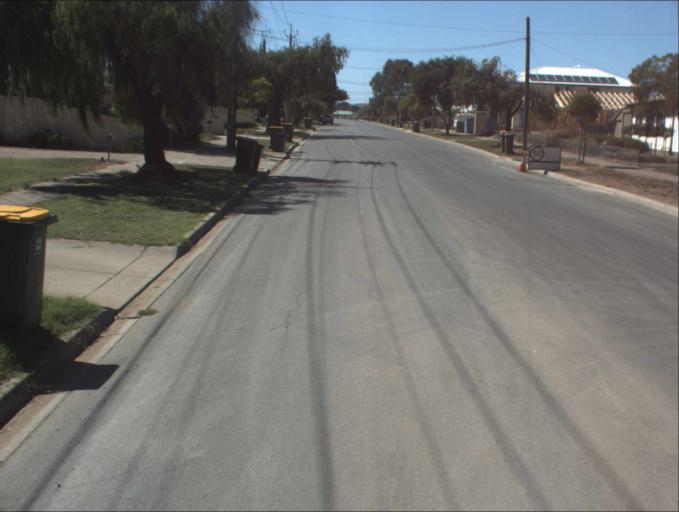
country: AU
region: South Australia
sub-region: Port Adelaide Enfield
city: Klemzig
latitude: -34.8662
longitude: 138.6200
